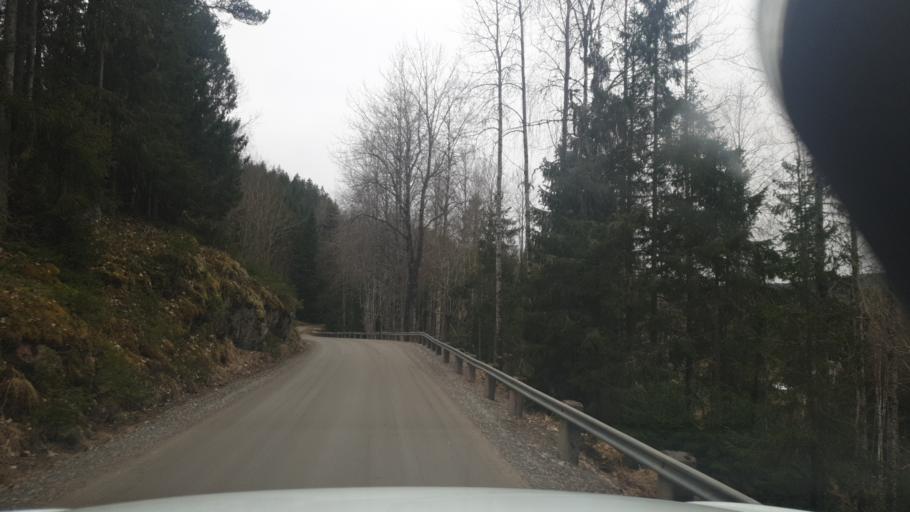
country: NO
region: Ostfold
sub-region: Romskog
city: Romskog
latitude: 59.7104
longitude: 11.9692
